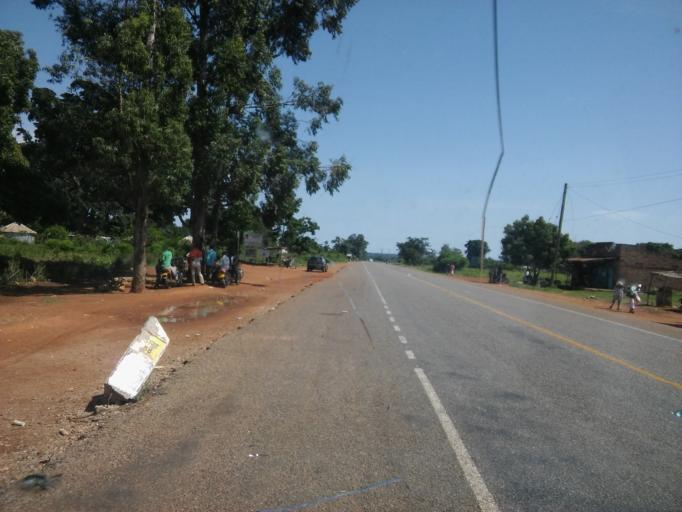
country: UG
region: Eastern Region
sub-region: Kumi District
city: Kumi
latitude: 1.4093
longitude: 33.9942
